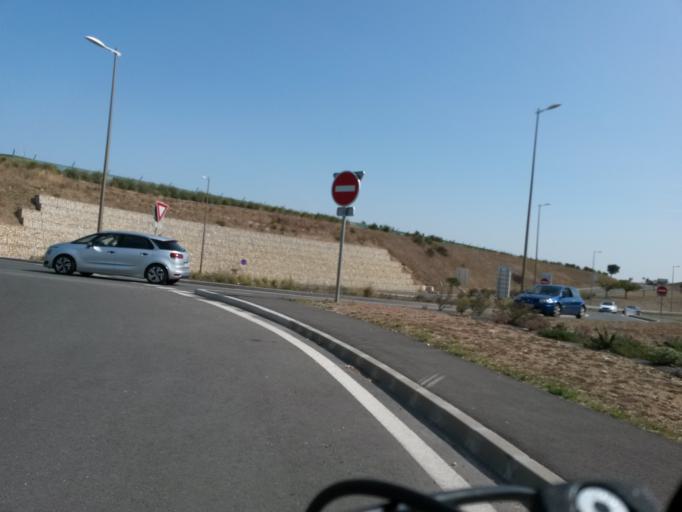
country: FR
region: Poitou-Charentes
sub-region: Departement de la Charente-Maritime
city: Rivedoux-Plage
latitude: 46.1753
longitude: -1.2156
